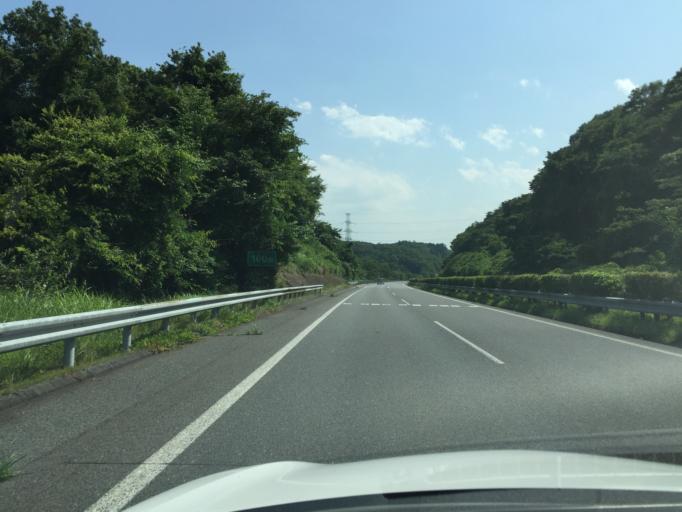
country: JP
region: Fukushima
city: Iwaki
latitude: 36.9567
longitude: 140.7803
